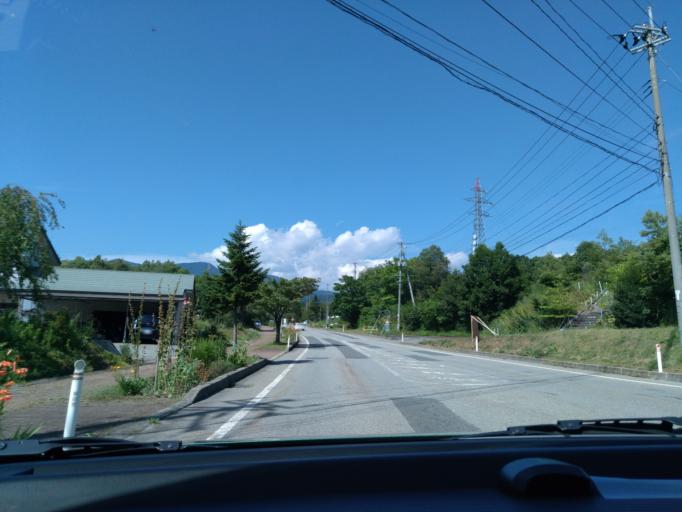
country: JP
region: Akita
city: Kakunodatemachi
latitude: 39.7423
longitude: 140.7195
